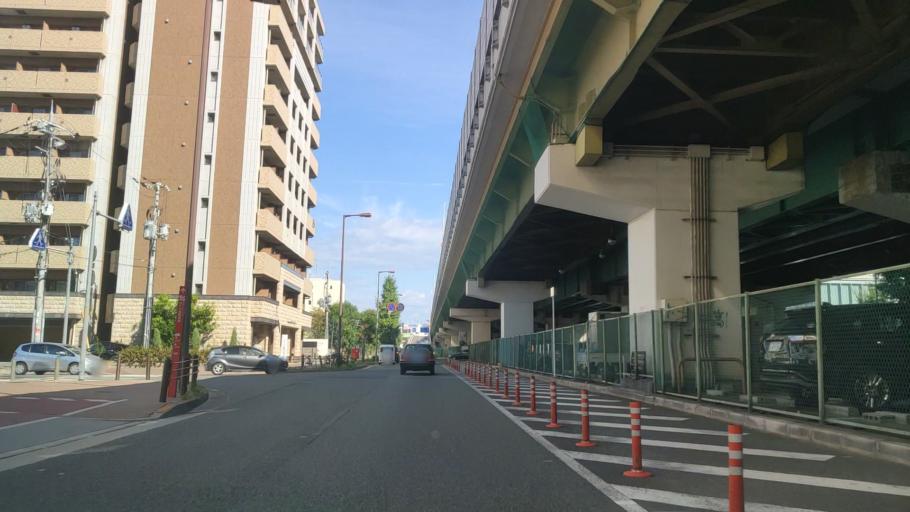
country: JP
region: Osaka
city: Suita
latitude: 34.7453
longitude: 135.4977
